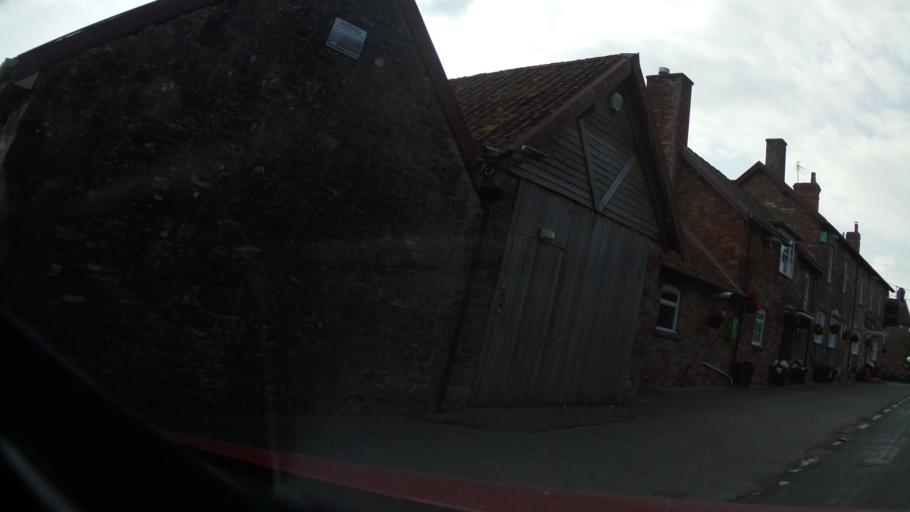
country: GB
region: England
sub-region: Bath and North East Somerset
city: Compton Martin
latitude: 51.3172
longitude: -2.6374
